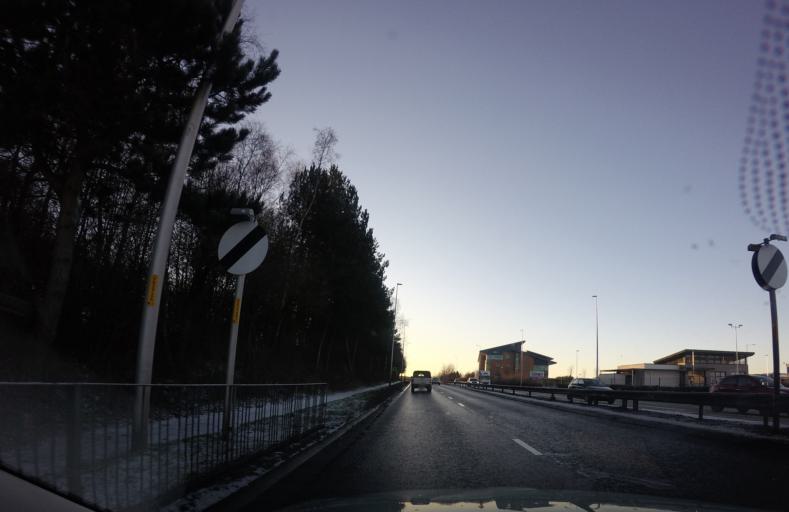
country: GB
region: Scotland
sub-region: Angus
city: Muirhead
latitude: 56.4733
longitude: -3.0508
